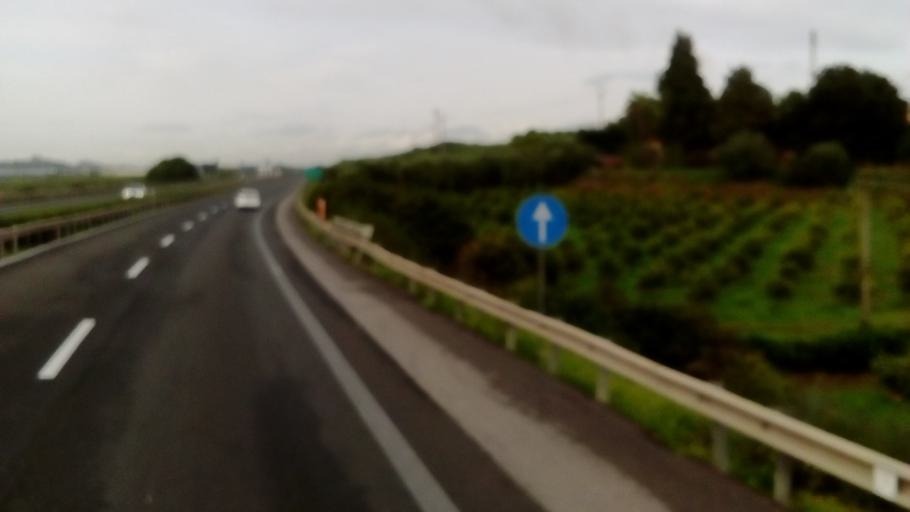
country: IT
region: Sicily
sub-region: Catania
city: Misterbianco
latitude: 37.4617
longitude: 15.0042
